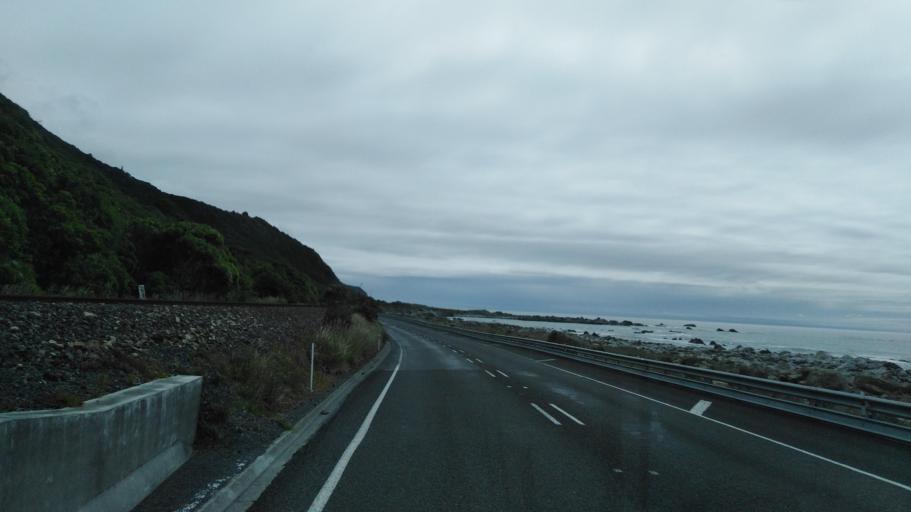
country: NZ
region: Canterbury
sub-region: Kaikoura District
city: Kaikoura
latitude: -42.2408
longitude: 173.8382
